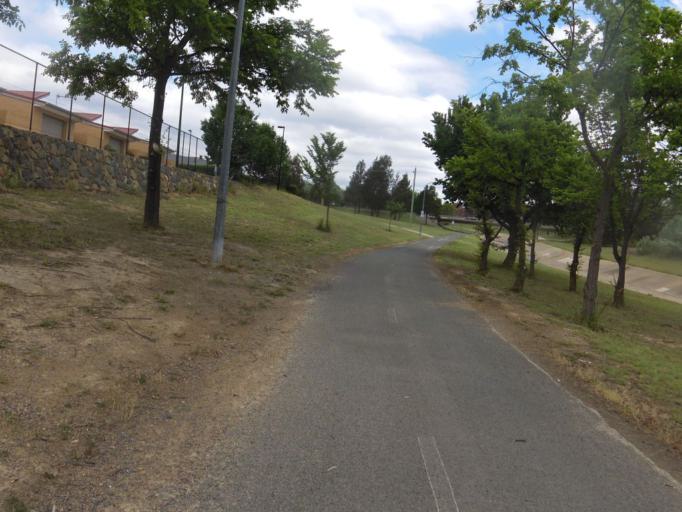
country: AU
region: Australian Capital Territory
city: Macarthur
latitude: -35.4206
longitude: 149.0935
